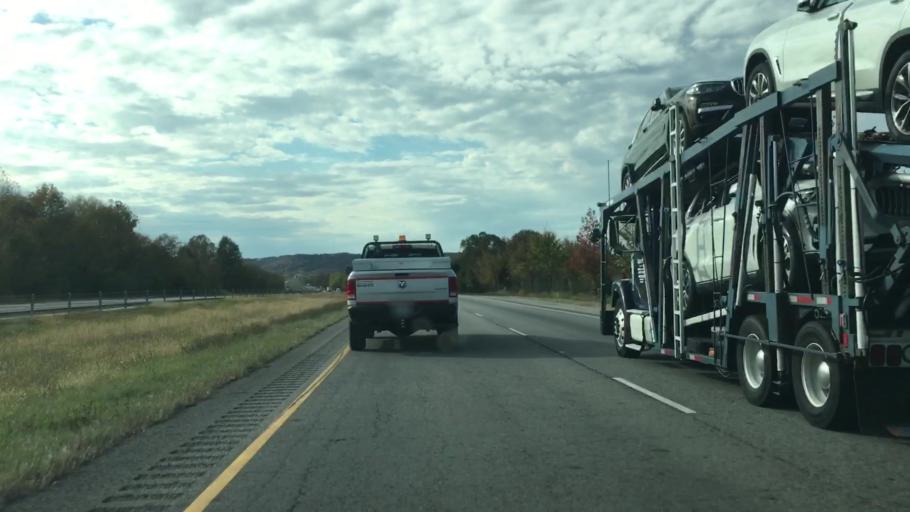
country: US
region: Arkansas
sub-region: Pope County
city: Atkins
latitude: 35.2513
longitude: -92.8916
